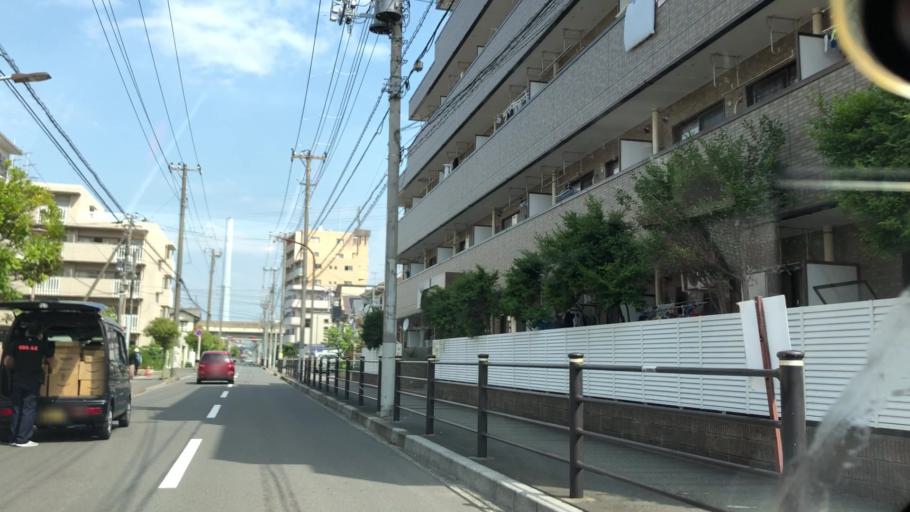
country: JP
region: Tokyo
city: Urayasu
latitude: 35.6780
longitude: 139.9115
